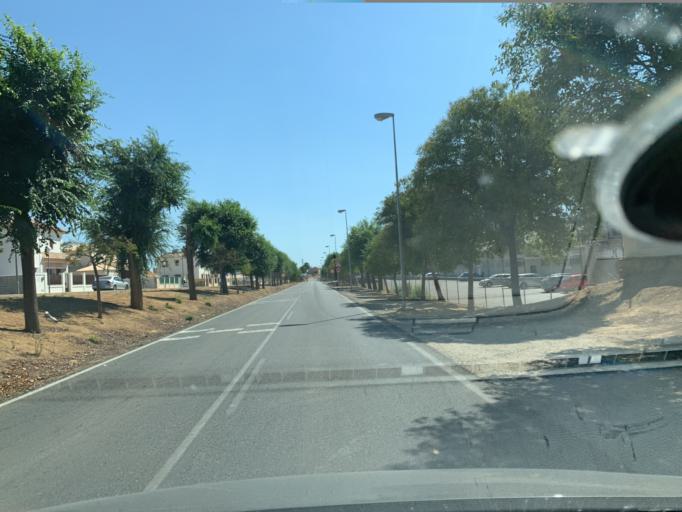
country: ES
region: Andalusia
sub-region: Provincia de Sevilla
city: Marchena
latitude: 37.3245
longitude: -5.4055
